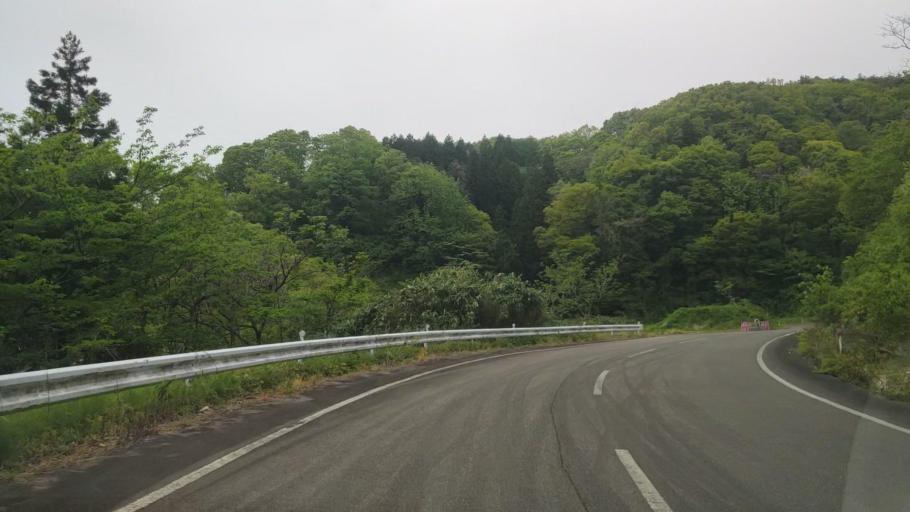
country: JP
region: Niigata
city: Kamo
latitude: 37.7118
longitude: 139.0929
